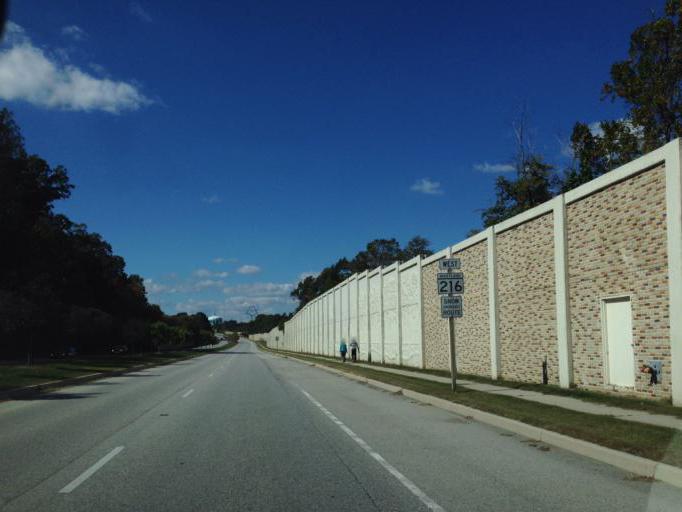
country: US
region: Maryland
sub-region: Howard County
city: North Laurel
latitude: 39.1412
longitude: -76.8776
